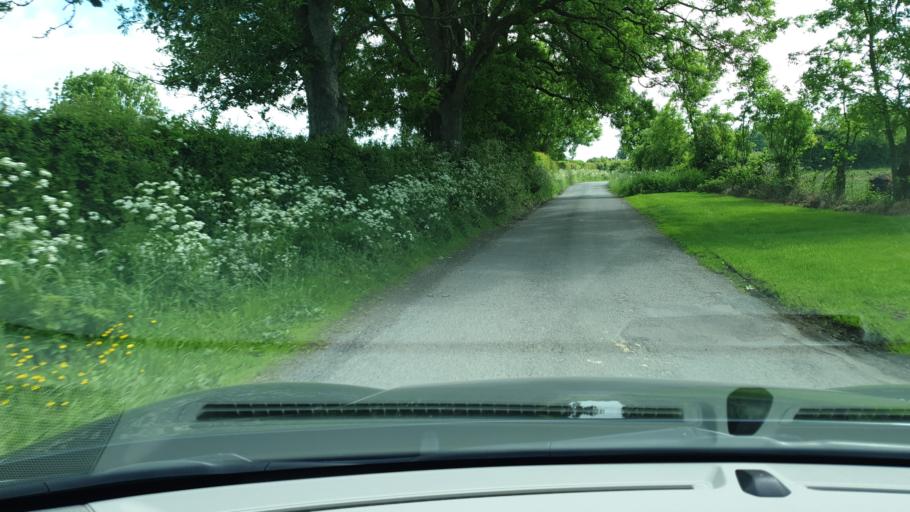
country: IE
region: Ulster
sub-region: An Cabhan
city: Kingscourt
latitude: 53.8005
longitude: -6.7210
